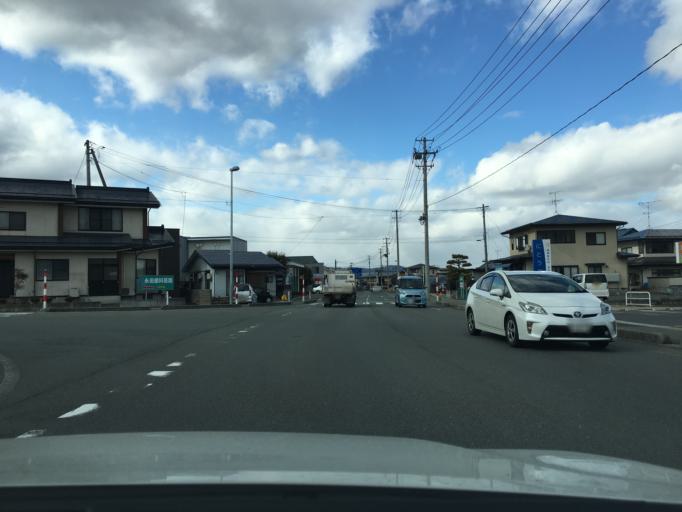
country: JP
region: Yamagata
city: Kaminoyama
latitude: 38.2057
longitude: 140.3086
